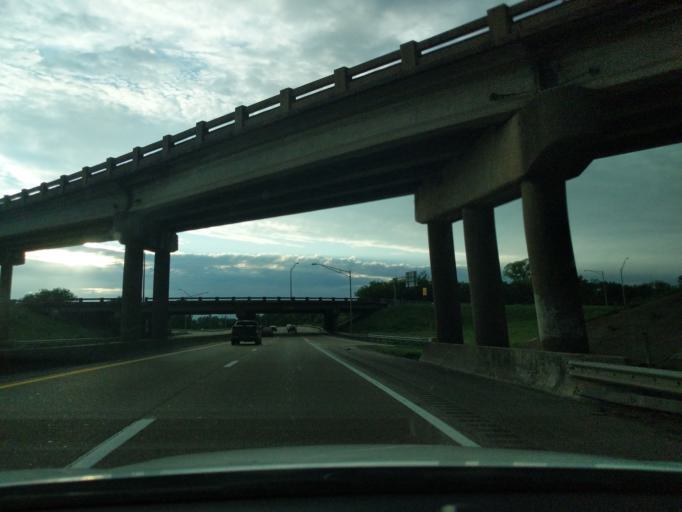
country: US
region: Tennessee
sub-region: Shelby County
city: New South Memphis
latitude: 35.0790
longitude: -90.0561
